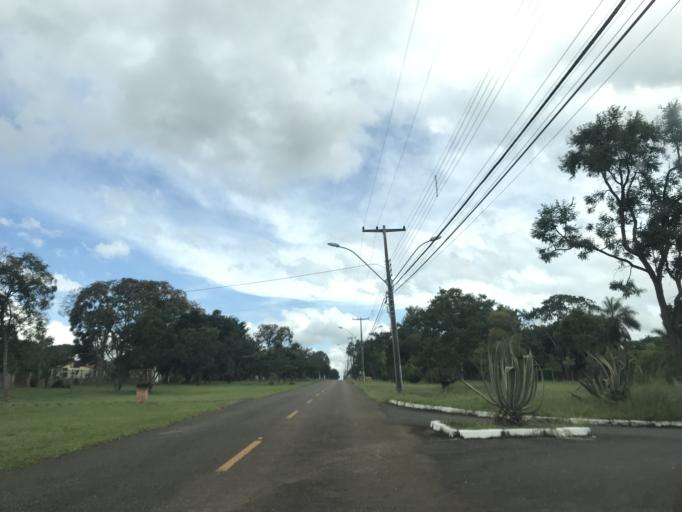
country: BR
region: Federal District
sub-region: Brasilia
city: Brasilia
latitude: -15.8896
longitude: -47.9247
